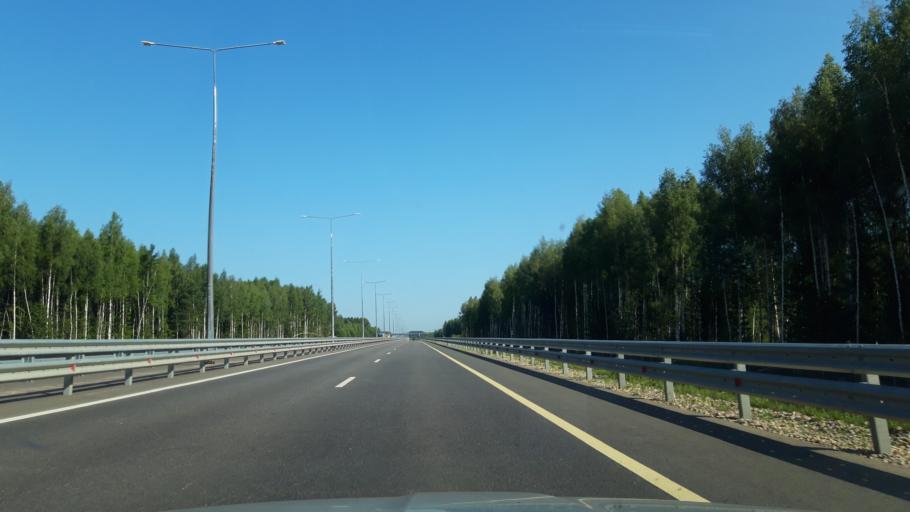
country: RU
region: Tverskaya
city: Zavidovo
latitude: 56.5377
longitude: 36.4946
